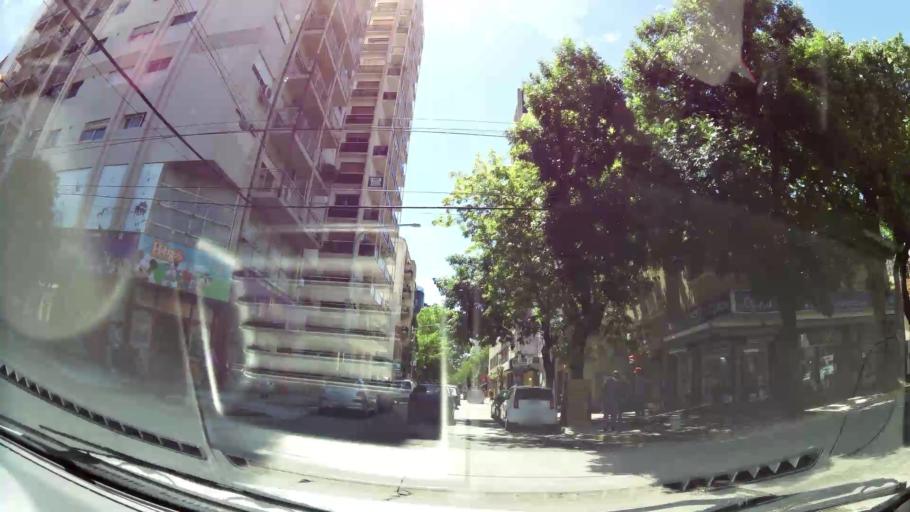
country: AR
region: Buenos Aires
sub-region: Partido de Quilmes
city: Quilmes
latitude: -34.7215
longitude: -58.2604
